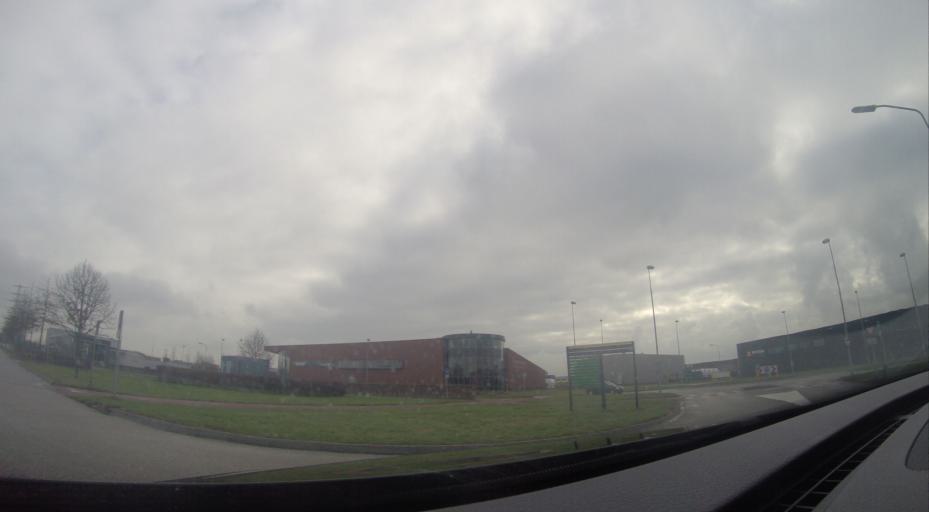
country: NL
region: Gelderland
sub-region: Gemeente Doetinchem
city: Doetinchem
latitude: 51.9490
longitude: 6.2773
